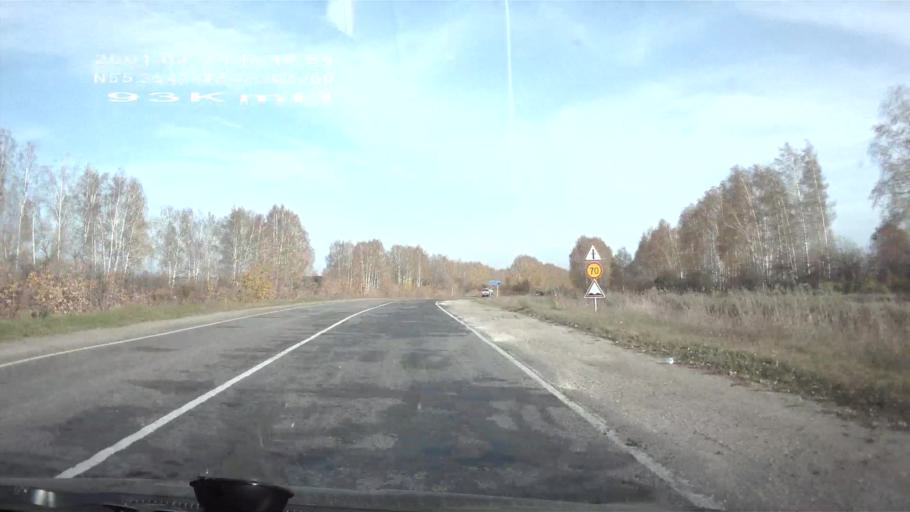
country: RU
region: Chuvashia
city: Ibresi
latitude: 55.3546
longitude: 47.2023
